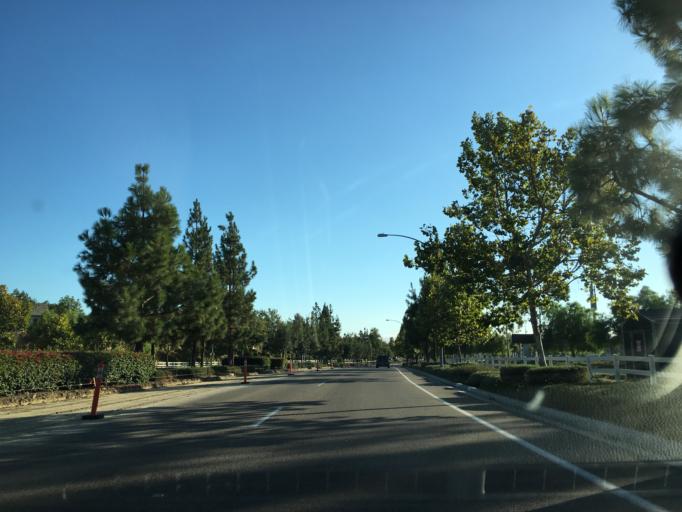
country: US
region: California
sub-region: San Diego County
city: Fairbanks Ranch
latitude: 32.9652
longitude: -117.1480
